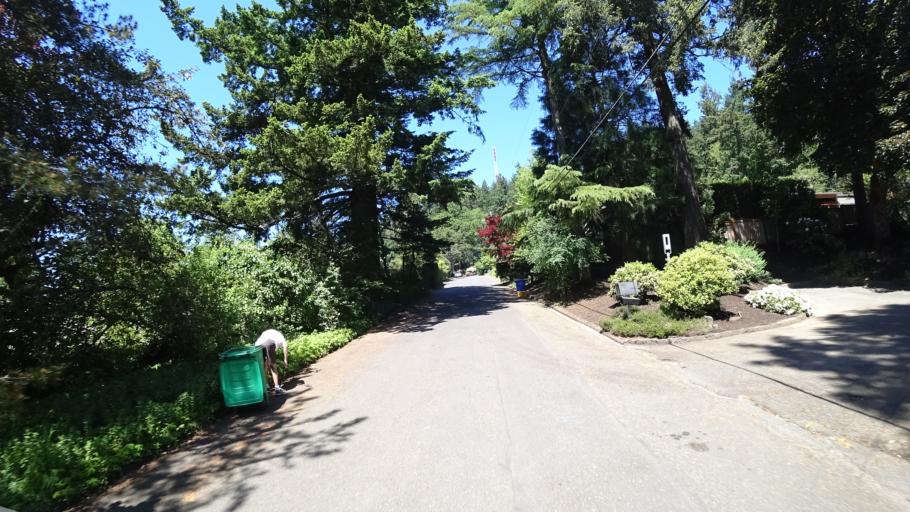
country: US
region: Oregon
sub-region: Multnomah County
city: Portland
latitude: 45.4950
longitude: -122.7095
